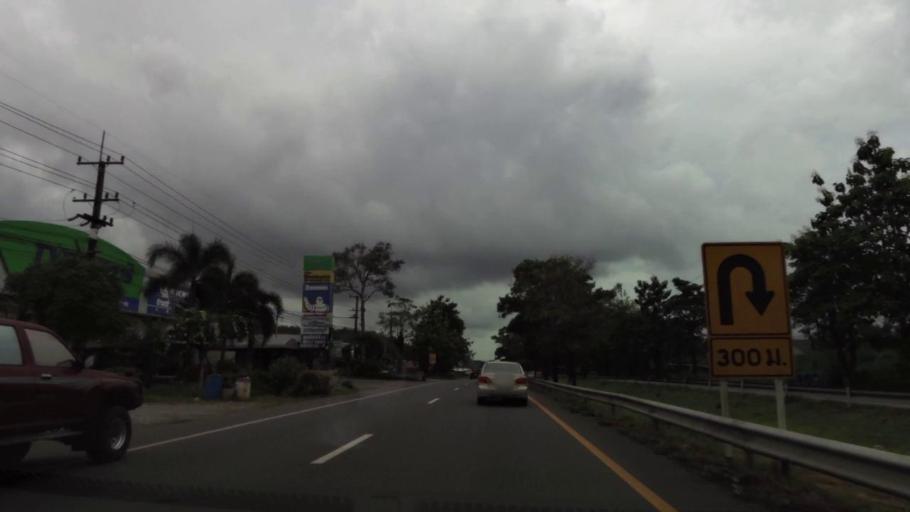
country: TH
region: Chanthaburi
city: Tha Mai
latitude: 12.6568
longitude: 102.0573
